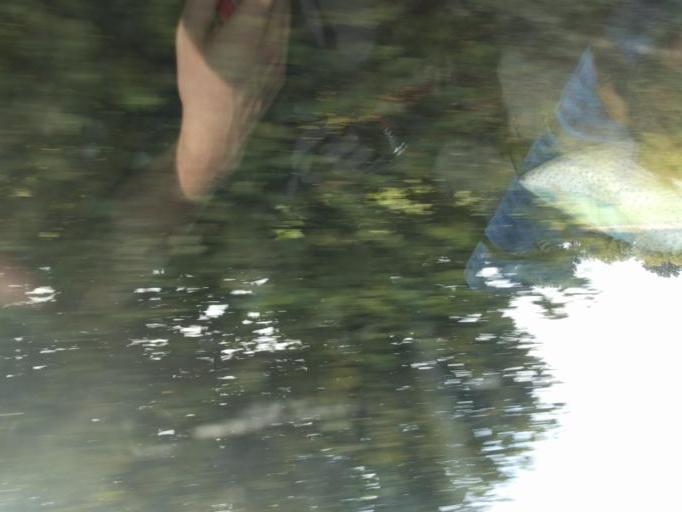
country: DE
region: Schleswig-Holstein
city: Hamberge
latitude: 53.8312
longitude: 10.5751
